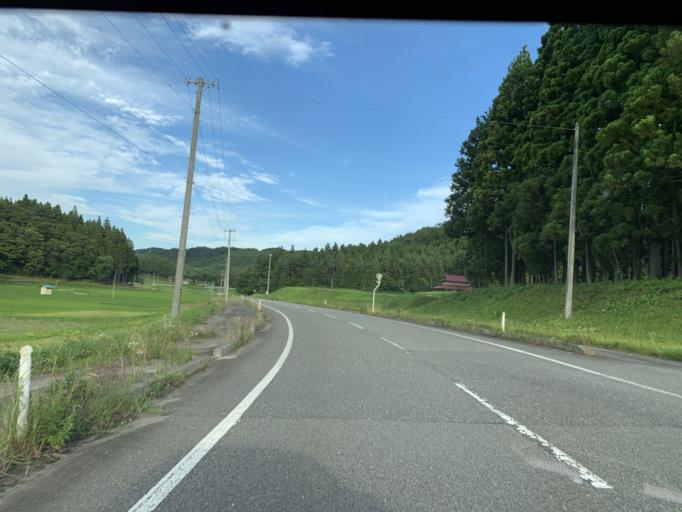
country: JP
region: Iwate
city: Ichinoseki
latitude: 38.8845
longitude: 140.9662
